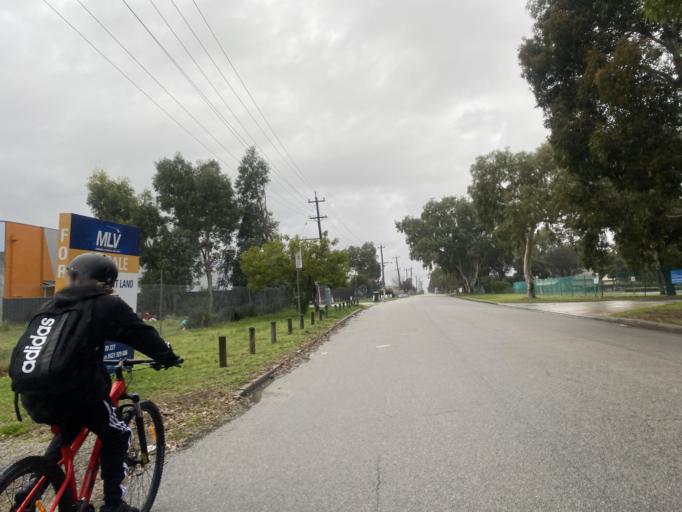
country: AU
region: Western Australia
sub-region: Canning
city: Queens Park
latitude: -31.9976
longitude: 115.9563
